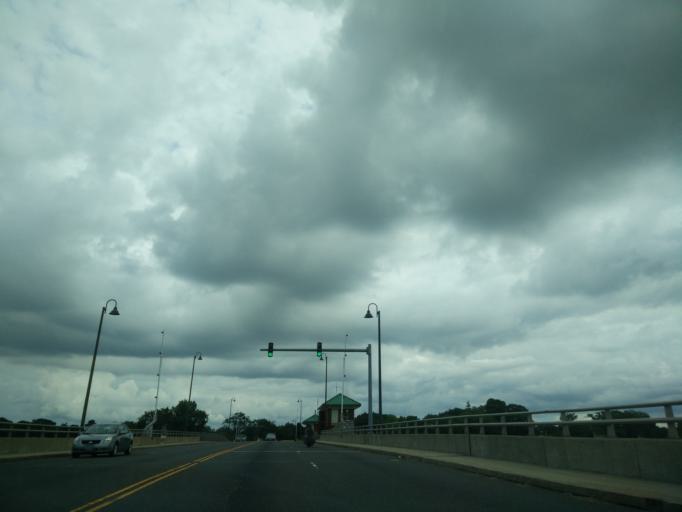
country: US
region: Connecticut
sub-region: Fairfield County
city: Stratford
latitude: 41.2006
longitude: -73.1120
